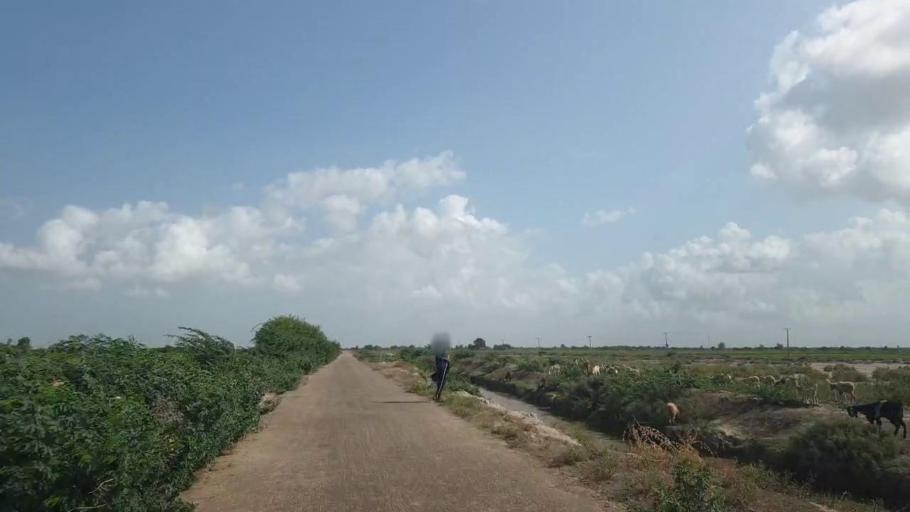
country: PK
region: Sindh
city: Kadhan
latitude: 24.5721
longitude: 69.0673
